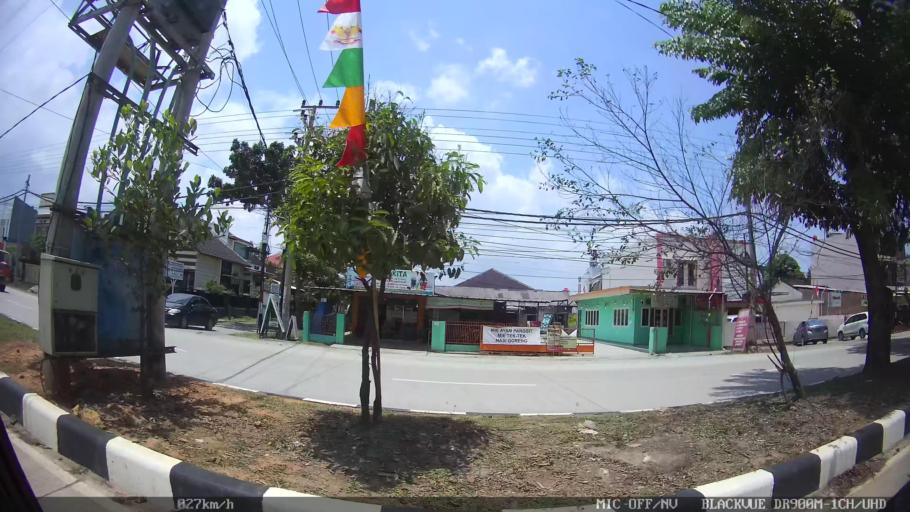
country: ID
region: Lampung
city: Kedaton
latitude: -5.3712
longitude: 105.2980
